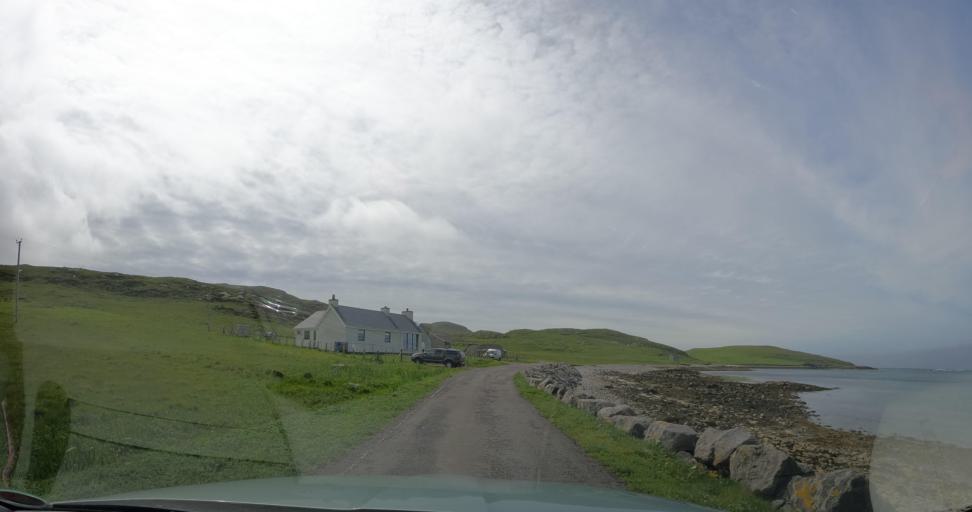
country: GB
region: Scotland
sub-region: Eilean Siar
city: Barra
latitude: 56.9452
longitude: -7.5395
